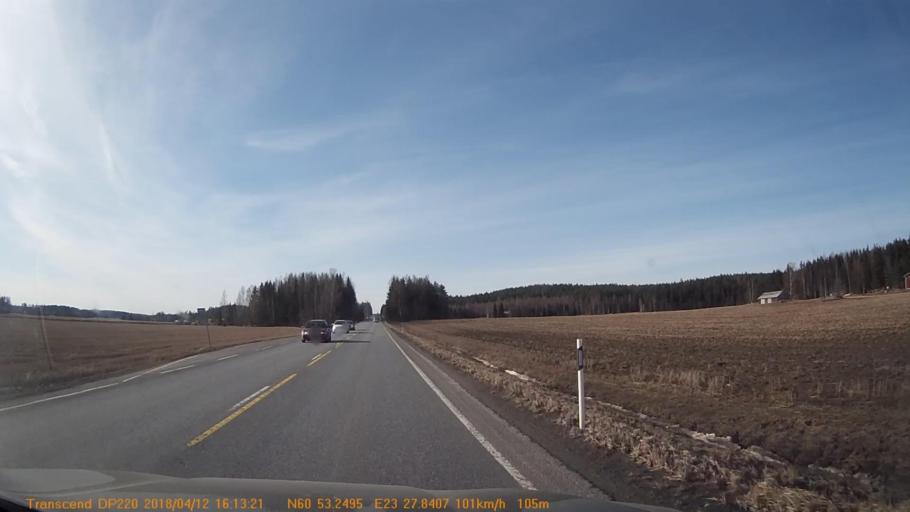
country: FI
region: Haeme
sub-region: Forssa
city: Jokioinen
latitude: 60.8876
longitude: 23.4637
